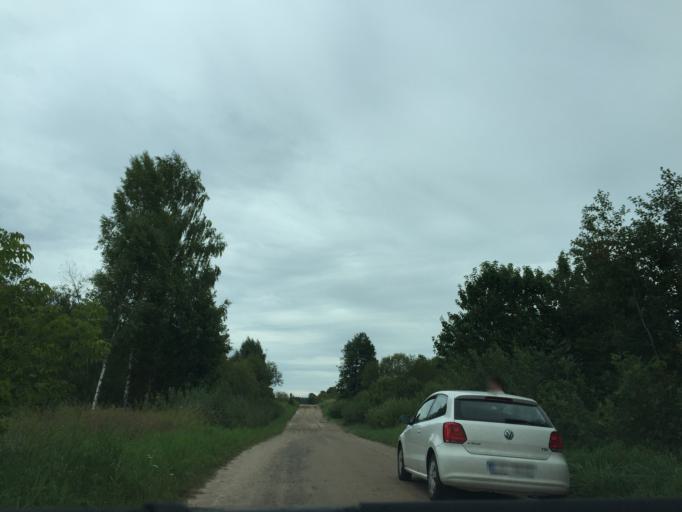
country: LV
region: Preilu Rajons
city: Jaunaglona
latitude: 56.2697
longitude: 27.0714
